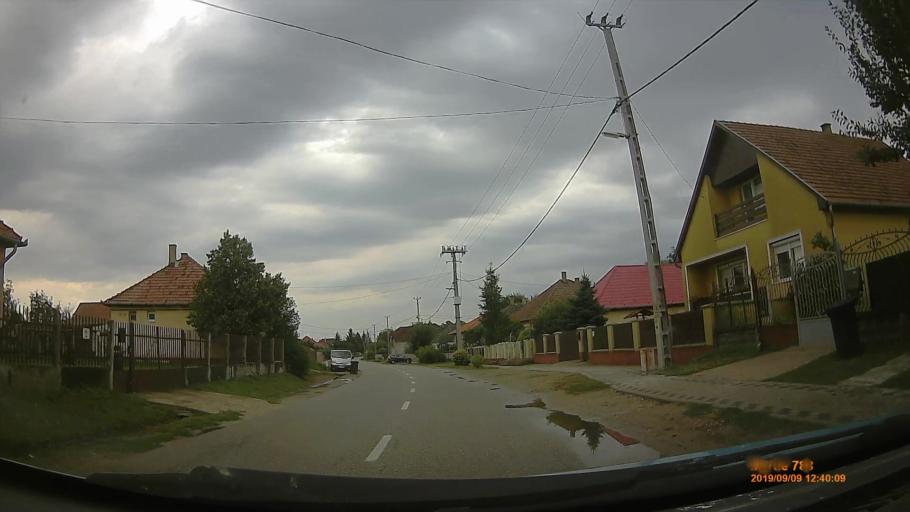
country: HU
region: Szabolcs-Szatmar-Bereg
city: Nyirpazony
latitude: 47.9871
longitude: 21.8004
